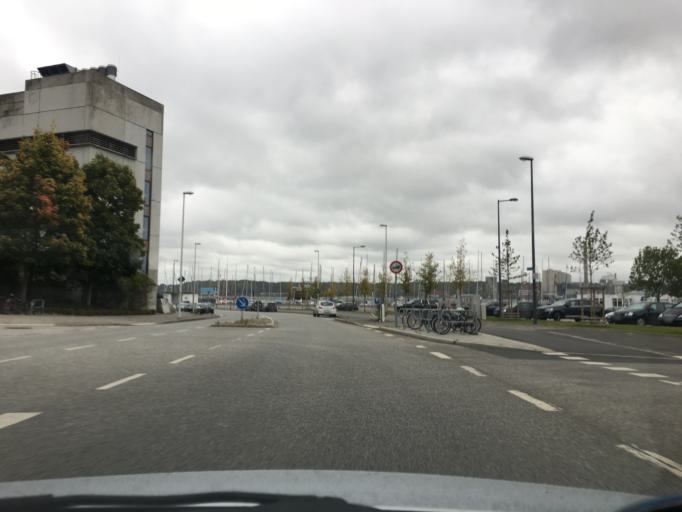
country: DE
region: Schleswig-Holstein
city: Kiel
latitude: 54.3377
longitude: 10.1555
